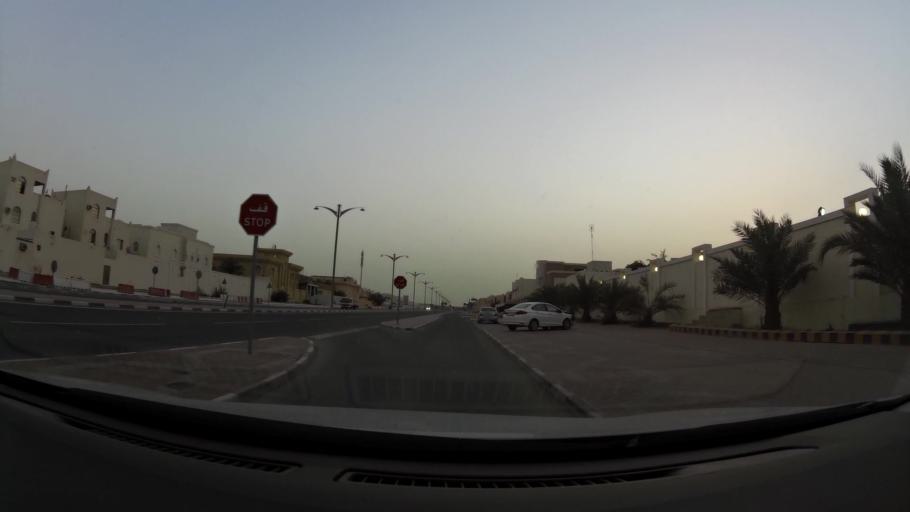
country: QA
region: Baladiyat ar Rayyan
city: Ar Rayyan
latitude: 25.2514
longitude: 51.4669
